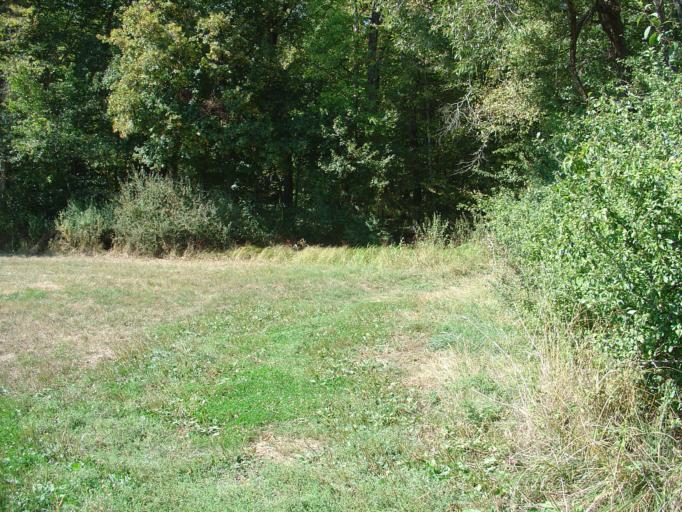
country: FR
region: Lorraine
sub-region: Departement de Meurthe-et-Moselle
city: Colombey-les-Belles
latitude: 48.5545
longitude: 5.8612
